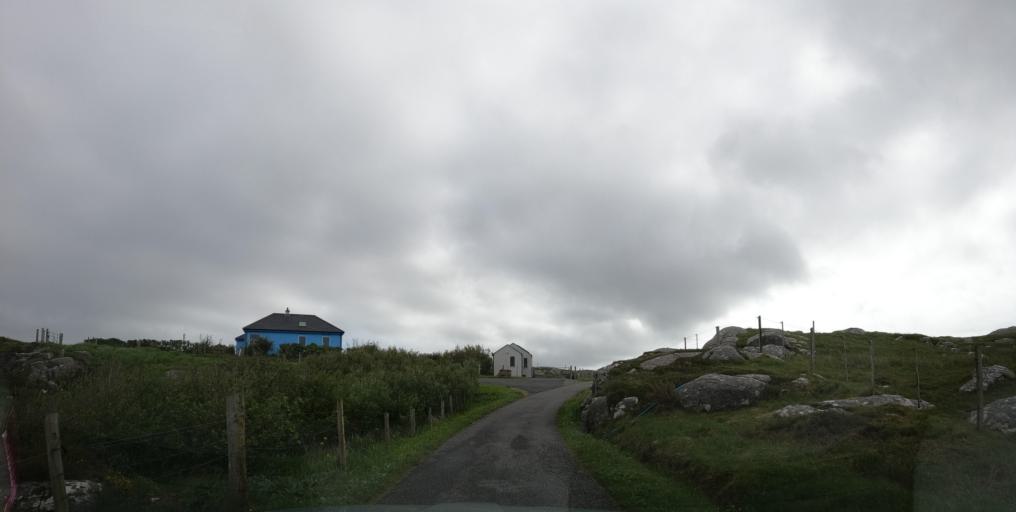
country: GB
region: Scotland
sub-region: Eilean Siar
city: Isle of South Uist
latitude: 57.0883
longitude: -7.2967
